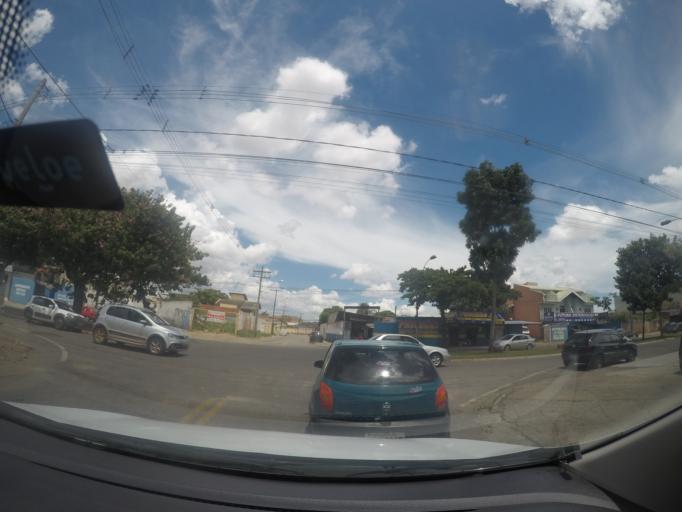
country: BR
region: Goias
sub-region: Goiania
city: Goiania
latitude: -16.6764
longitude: -49.3091
